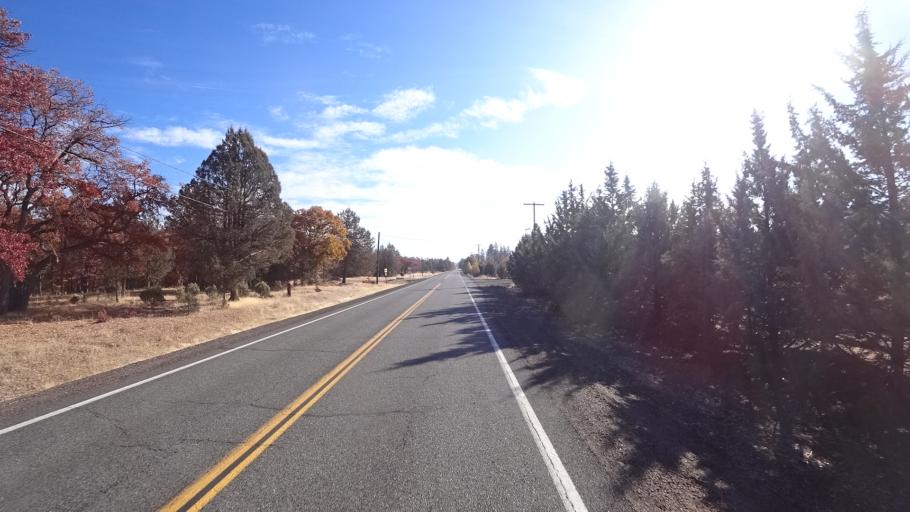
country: US
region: California
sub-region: Siskiyou County
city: Yreka
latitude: 41.6601
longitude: -122.5958
